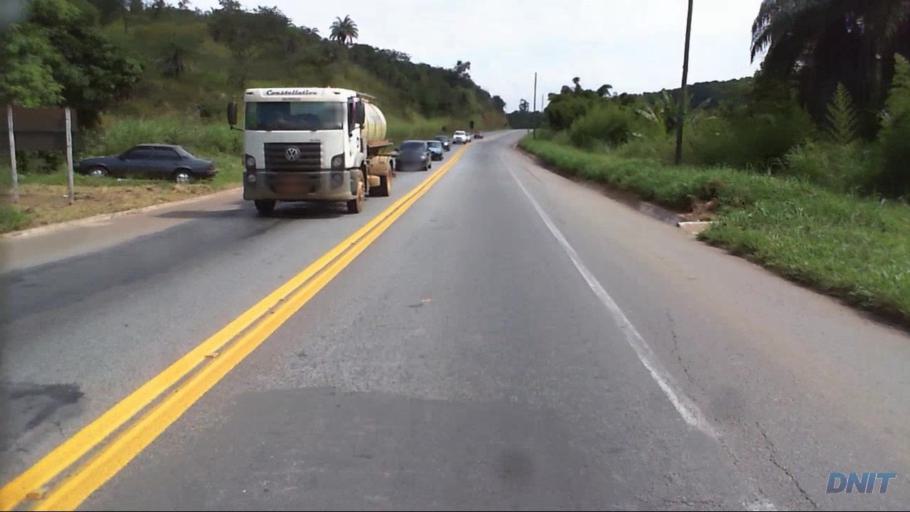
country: BR
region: Minas Gerais
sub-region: Santa Luzia
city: Santa Luzia
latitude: -19.8281
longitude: -43.8394
